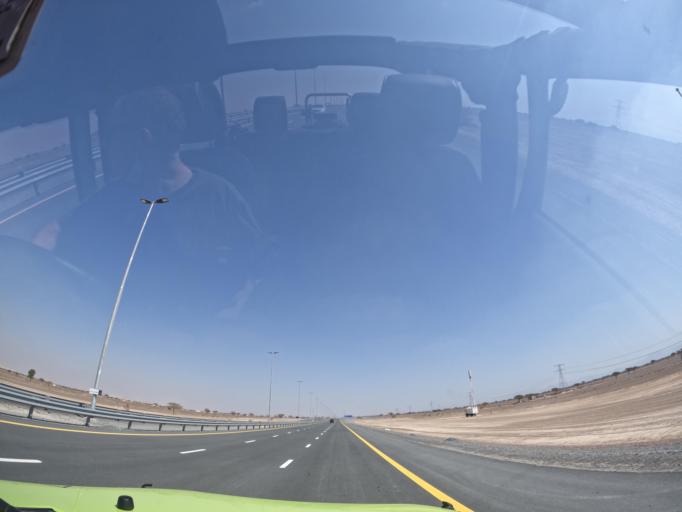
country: AE
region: Ash Shariqah
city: Adh Dhayd
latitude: 24.9489
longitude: 55.8332
